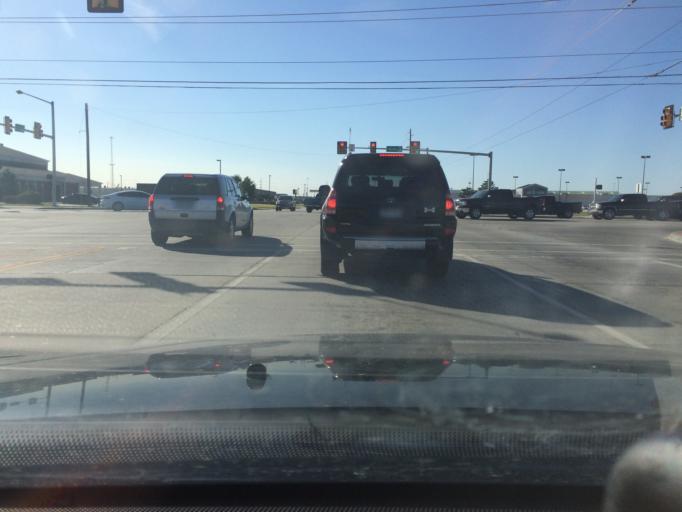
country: US
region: Oklahoma
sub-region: Tulsa County
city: Broken Arrow
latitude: 36.0900
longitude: -95.8506
